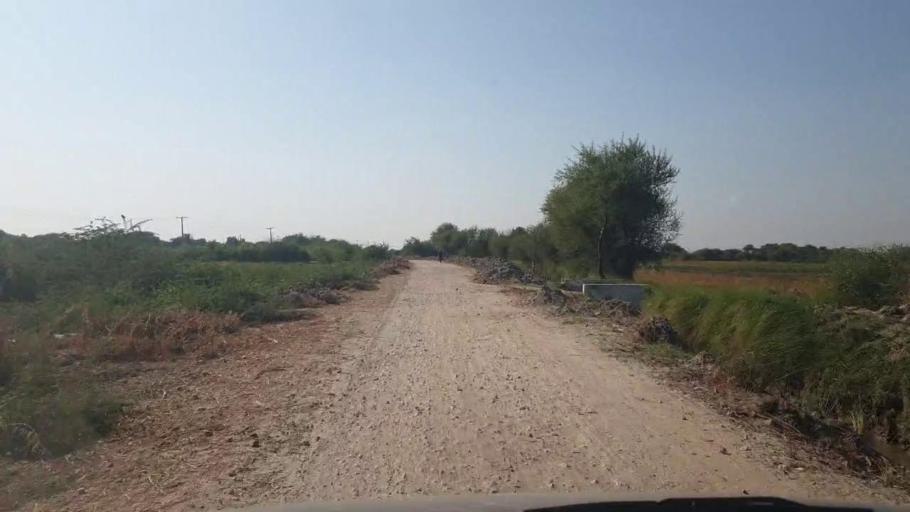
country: PK
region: Sindh
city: Badin
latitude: 24.5795
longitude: 68.7986
